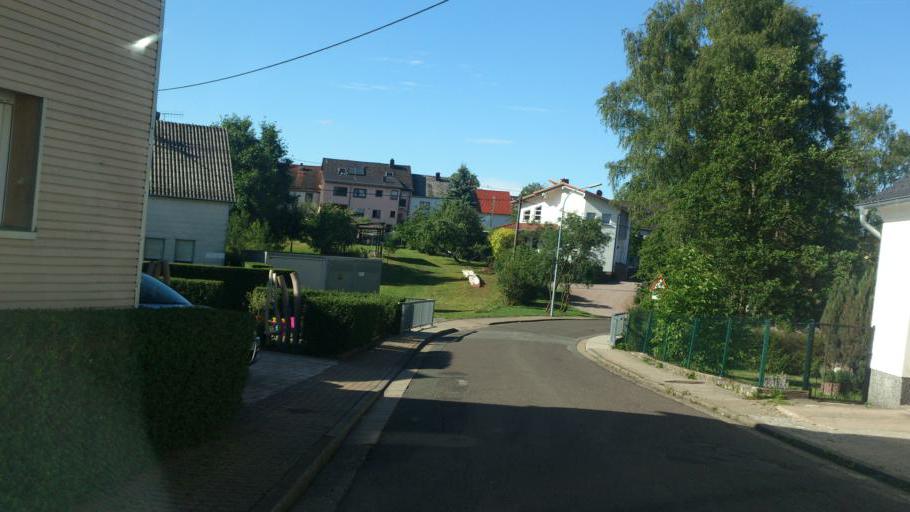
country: DE
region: Rheinland-Pfalz
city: Achtelsbach
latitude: 49.5701
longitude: 7.0493
